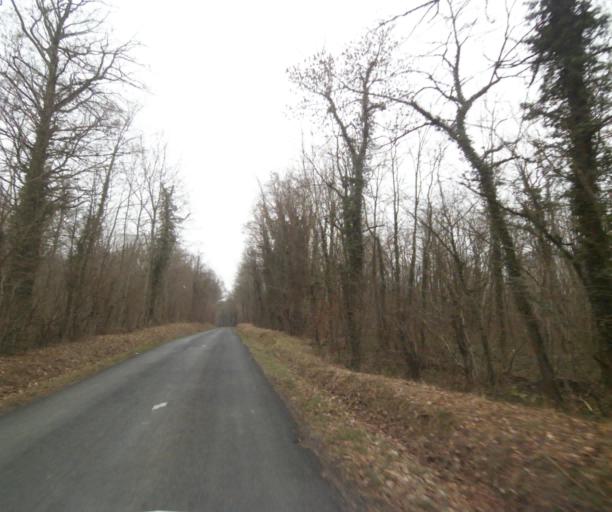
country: FR
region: Champagne-Ardenne
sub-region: Departement de la Haute-Marne
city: Bienville
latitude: 48.5679
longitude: 5.0183
